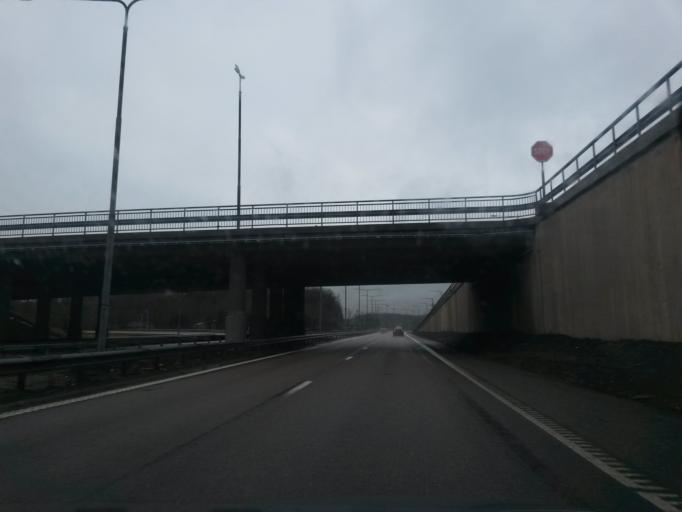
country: SE
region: Vaestra Goetaland
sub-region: Uddevalla Kommun
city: Uddevalla
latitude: 58.3546
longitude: 11.9640
